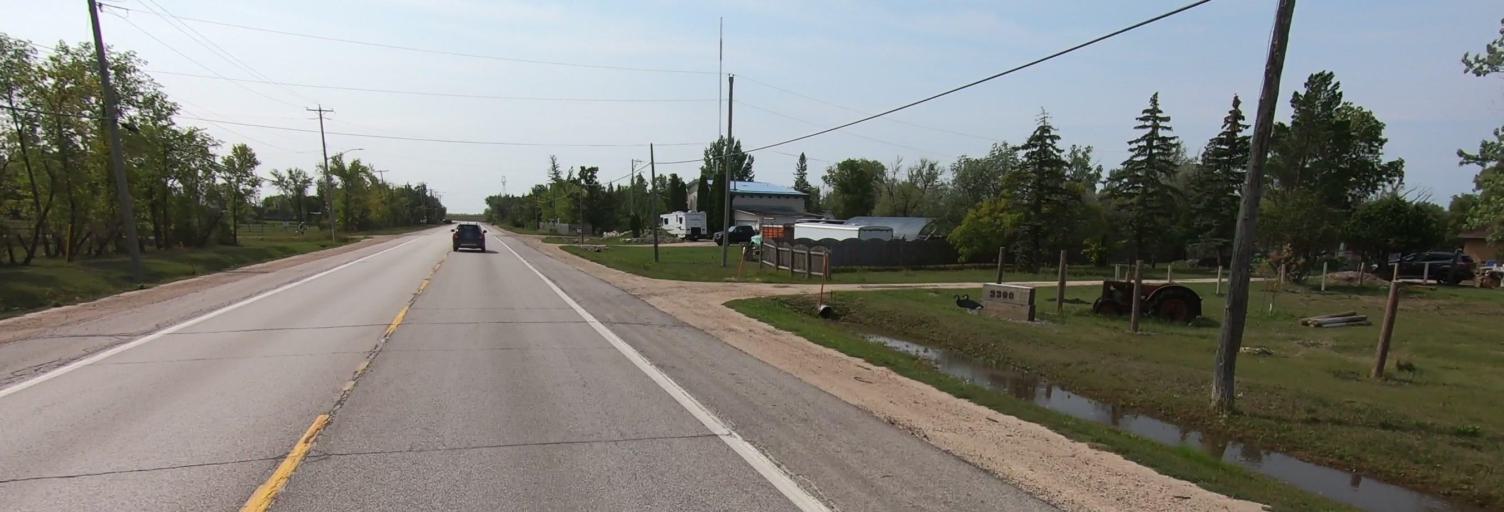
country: CA
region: Manitoba
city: Winnipeg
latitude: 49.7646
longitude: -97.1285
